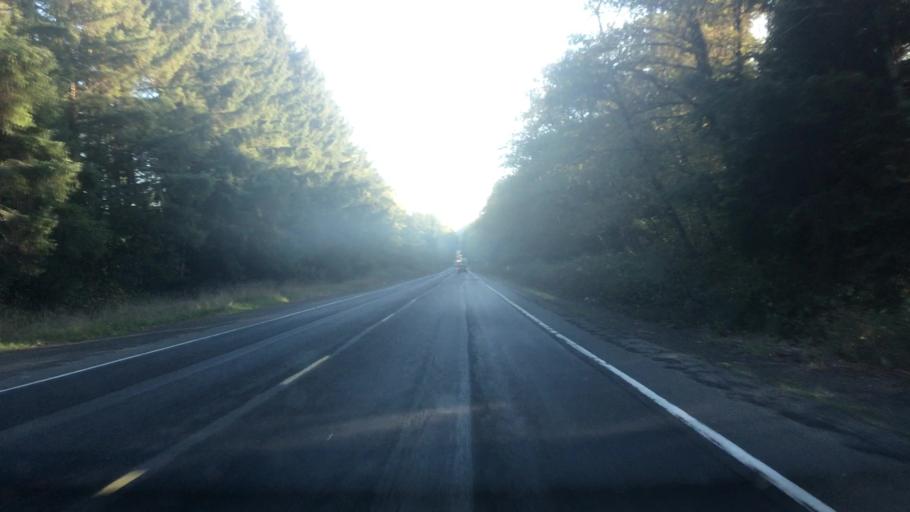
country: US
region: Oregon
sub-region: Clatsop County
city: Cannon Beach
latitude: 45.8977
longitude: -123.9546
